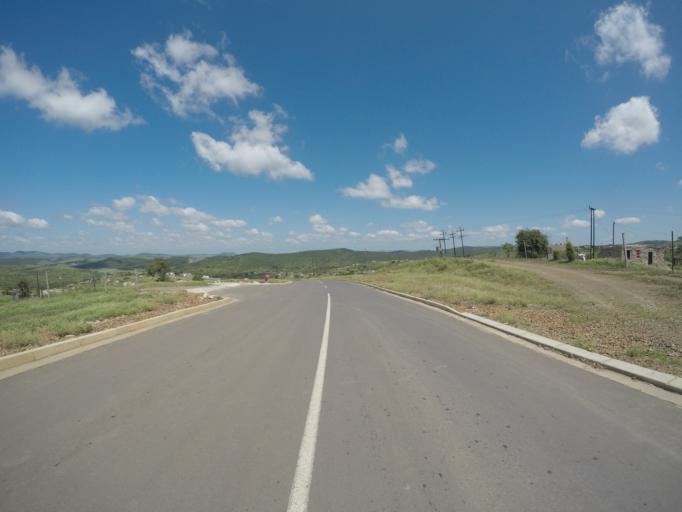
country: ZA
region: KwaZulu-Natal
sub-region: uThungulu District Municipality
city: Empangeni
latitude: -28.6089
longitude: 31.7466
